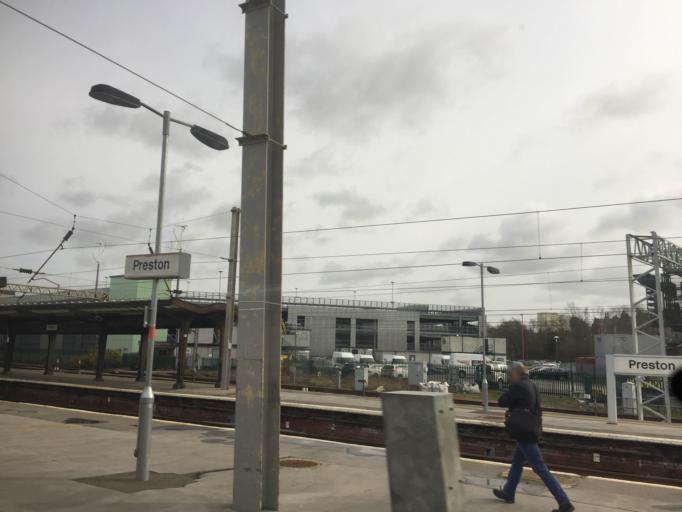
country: GB
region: England
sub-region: Lancashire
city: Preston
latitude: 53.7534
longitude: -2.7067
